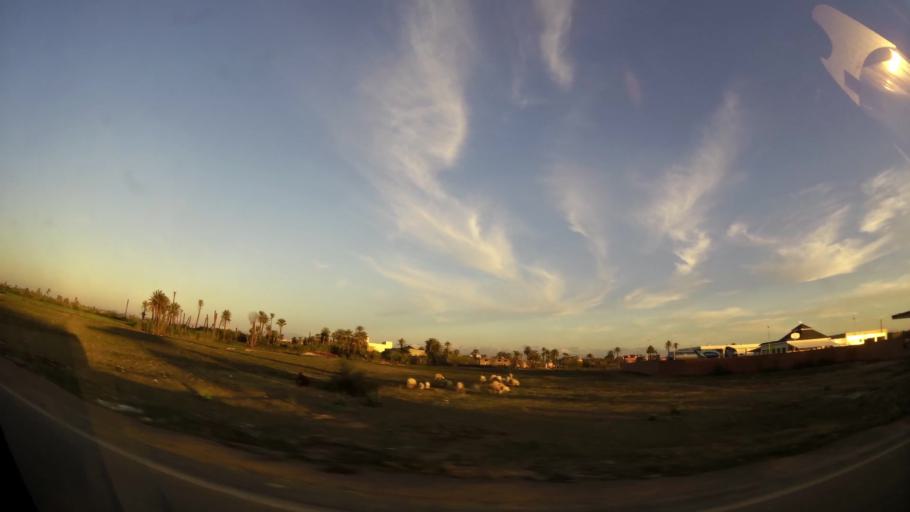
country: MA
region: Marrakech-Tensift-Al Haouz
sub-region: Marrakech
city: Marrakesh
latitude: 31.6857
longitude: -8.0365
